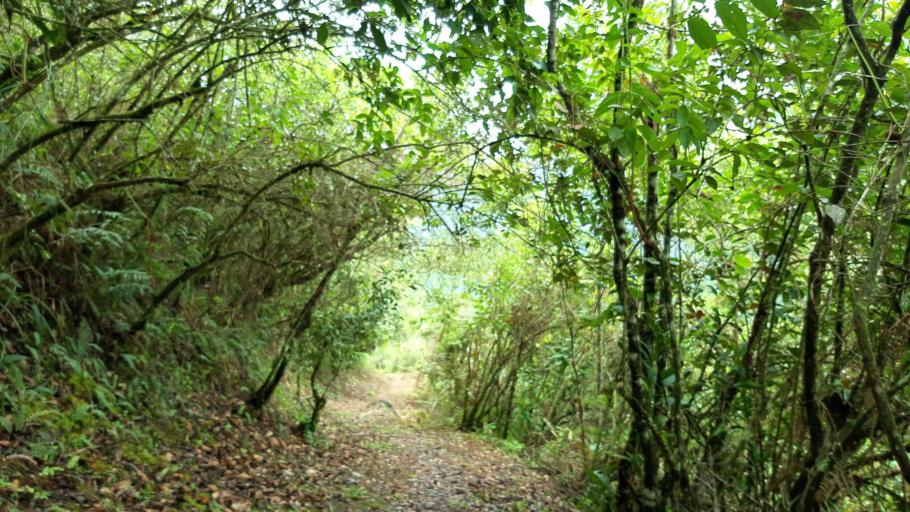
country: CO
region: Boyaca
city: Santa Maria
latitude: 4.9183
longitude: -73.3042
